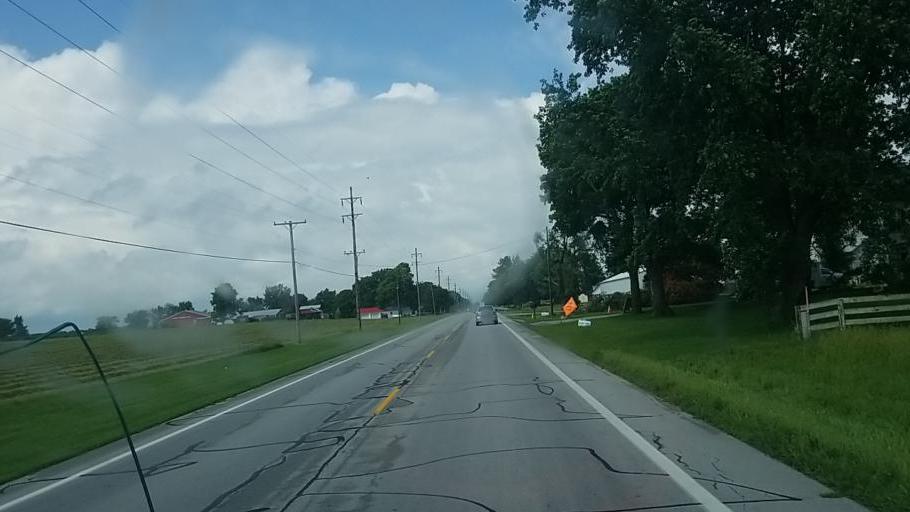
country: US
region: Ohio
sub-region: Champaign County
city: Urbana
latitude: 40.1713
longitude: -83.7441
